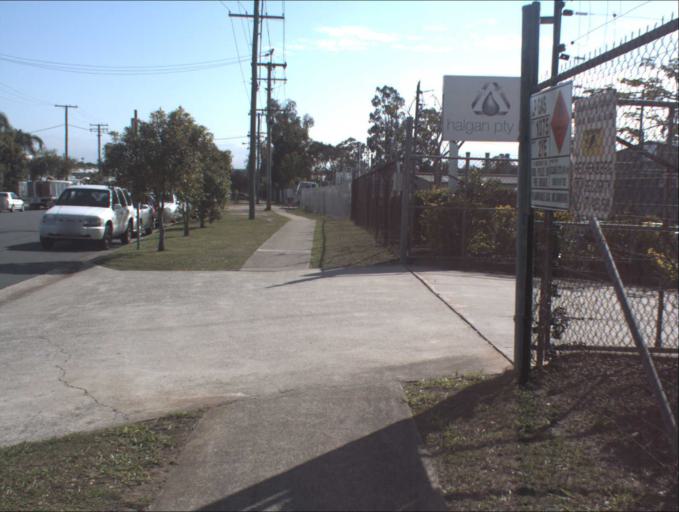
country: AU
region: Queensland
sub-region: Logan
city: Logan Reserve
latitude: -27.6872
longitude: 153.0775
